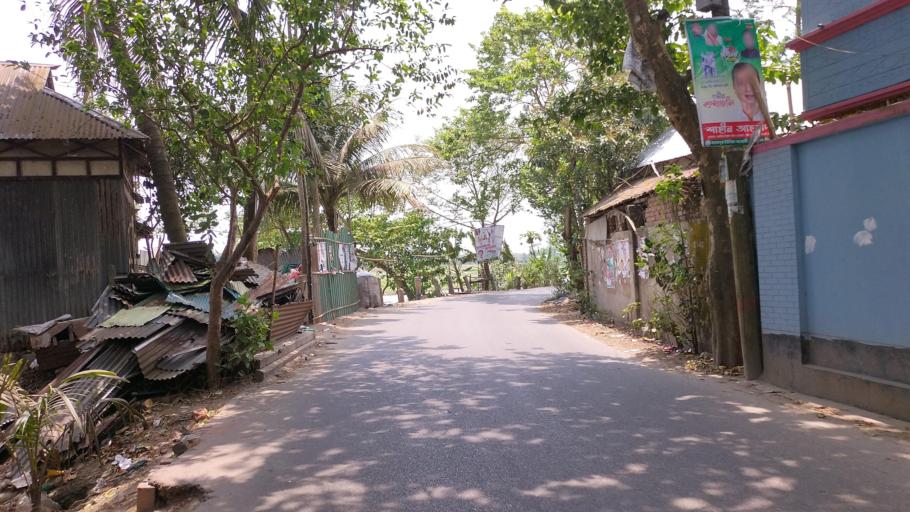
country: BD
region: Dhaka
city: Azimpur
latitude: 23.7416
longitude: 90.2495
